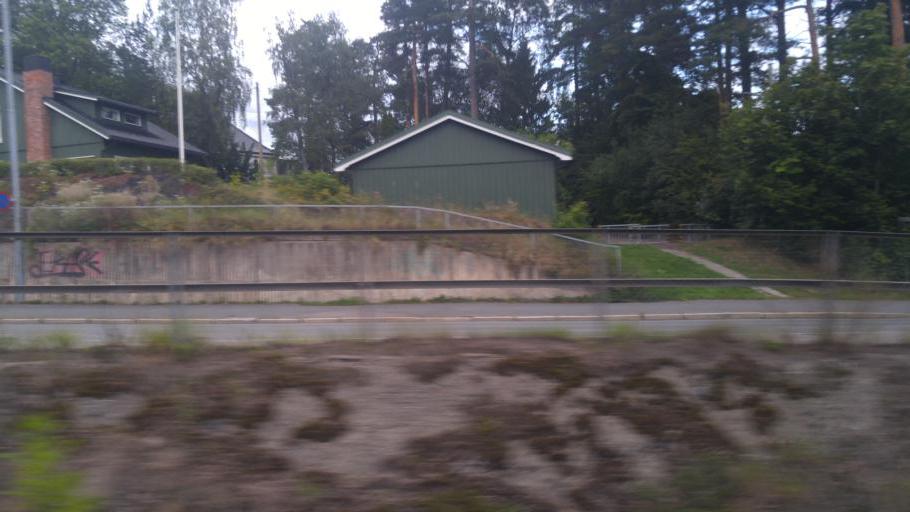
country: NO
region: Oslo
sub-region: Oslo
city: Sjolyststranda
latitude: 59.9496
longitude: 10.6962
